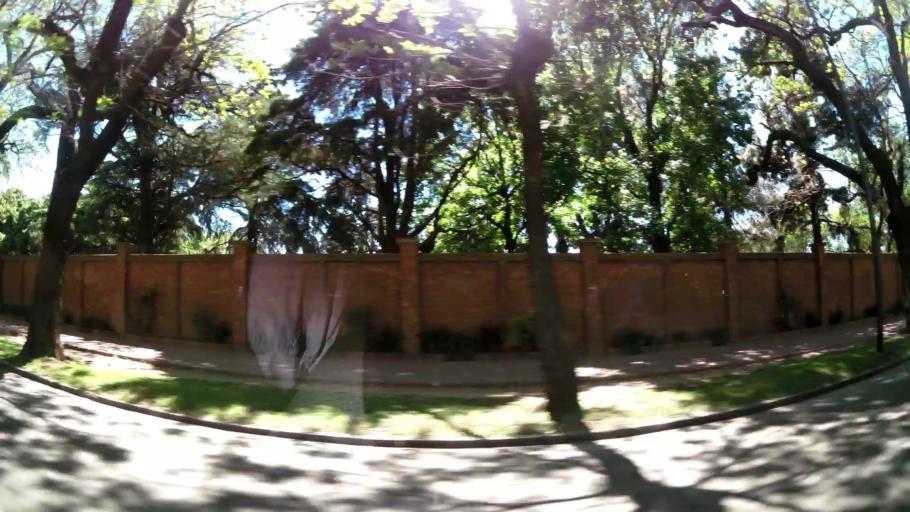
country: AR
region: Buenos Aires
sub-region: Partido de Vicente Lopez
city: Olivos
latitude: -34.5173
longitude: -58.4872
